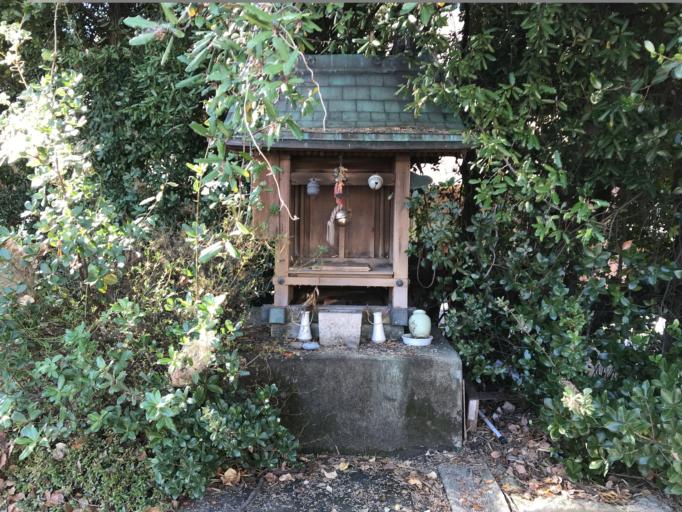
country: JP
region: Osaka
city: Tondabayashicho
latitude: 34.5186
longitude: 135.6096
